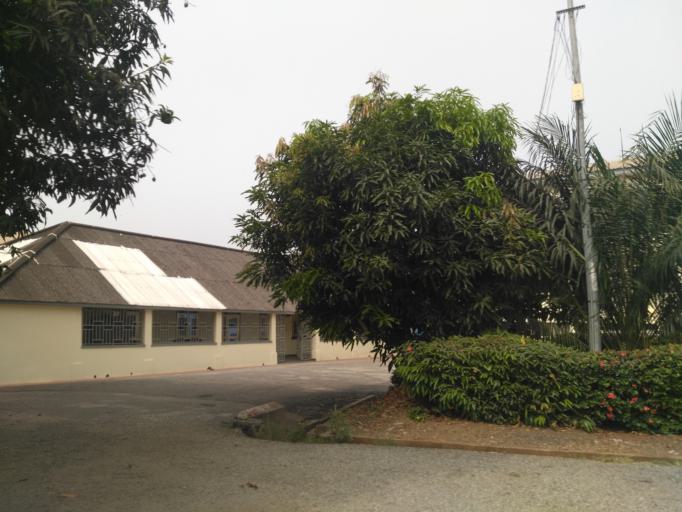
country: GH
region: Ashanti
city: Kumasi
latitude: 6.6901
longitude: -1.6259
